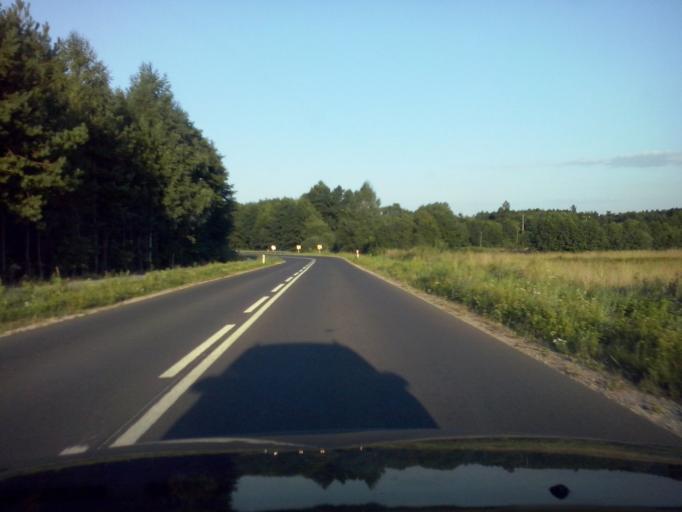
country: PL
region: Swietokrzyskie
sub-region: Powiat kielecki
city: Chmielnik
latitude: 50.6160
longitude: 20.7812
